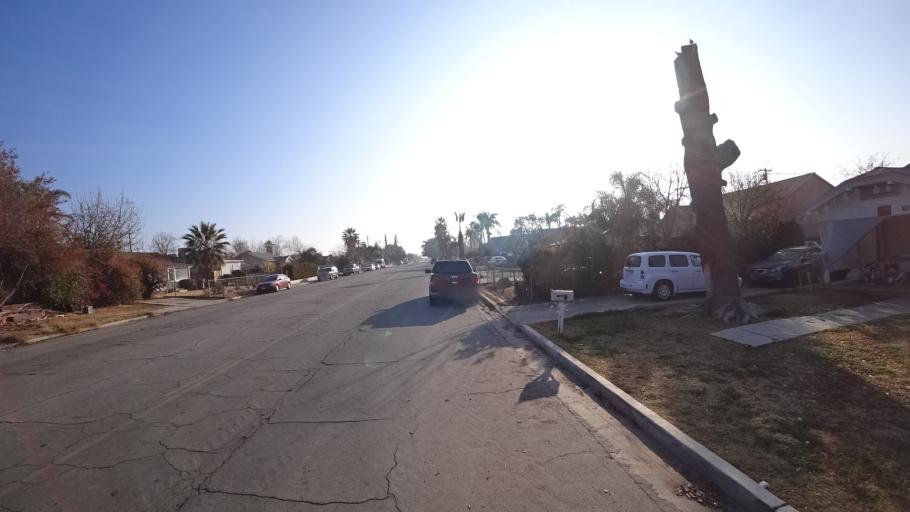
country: US
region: California
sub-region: Kern County
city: Bakersfield
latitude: 35.3756
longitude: -118.9742
